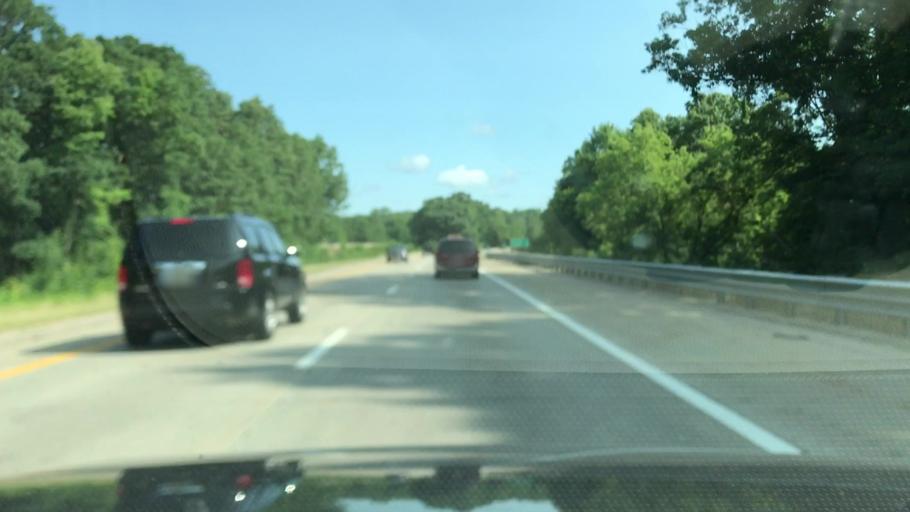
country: US
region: Michigan
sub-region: Kent County
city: Comstock Park
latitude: 43.0596
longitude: -85.6627
